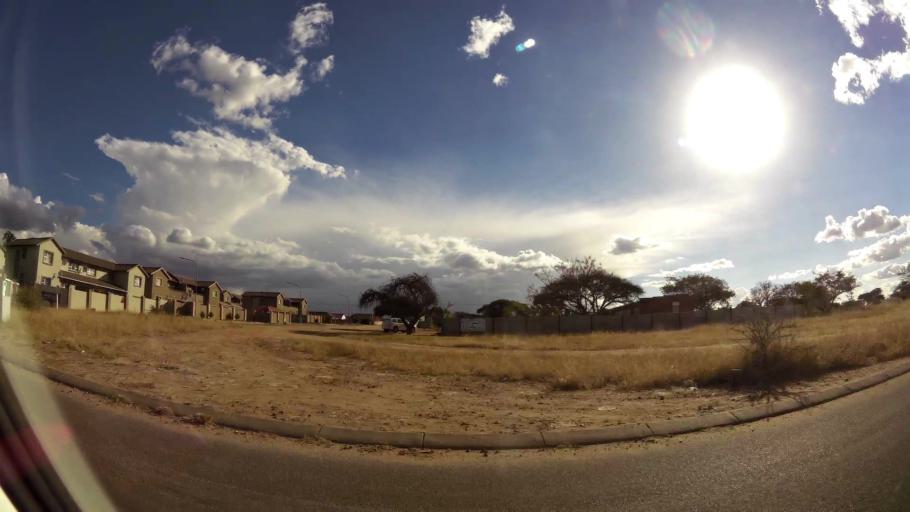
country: ZA
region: Limpopo
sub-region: Capricorn District Municipality
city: Polokwane
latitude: -23.9375
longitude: 29.4456
